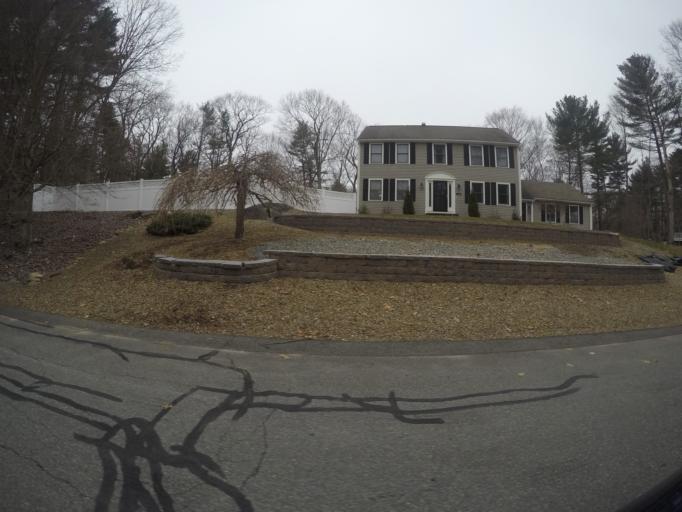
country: US
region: Massachusetts
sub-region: Bristol County
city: Easton
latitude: 42.0300
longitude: -71.1380
